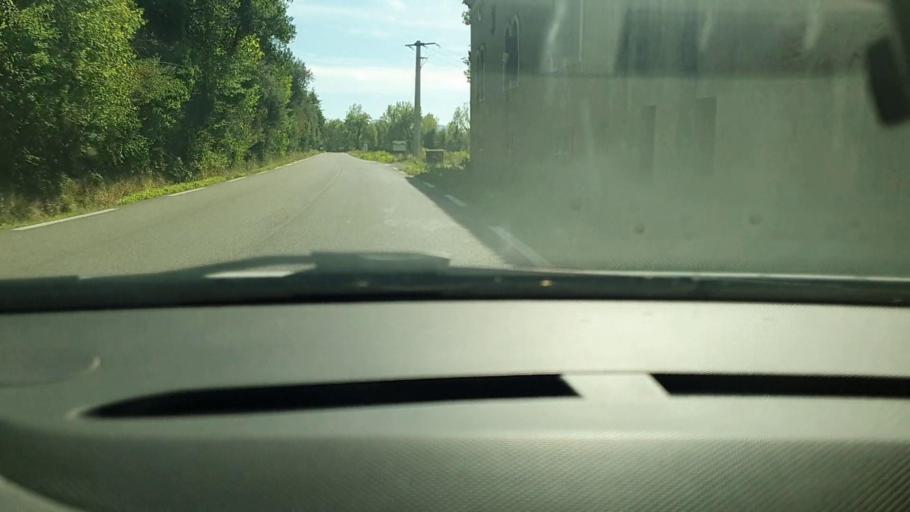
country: FR
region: Languedoc-Roussillon
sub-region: Departement du Gard
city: Saint-Ambroix
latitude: 44.2439
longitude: 4.2191
